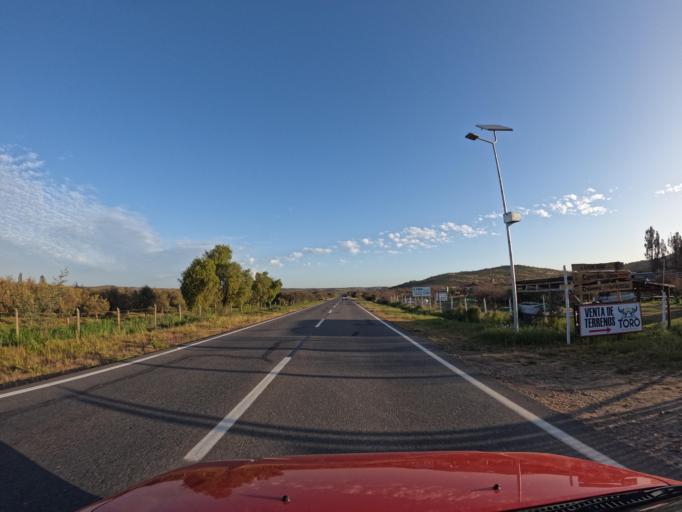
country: CL
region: O'Higgins
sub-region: Provincia de Colchagua
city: Santa Cruz
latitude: -34.2788
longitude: -71.7303
